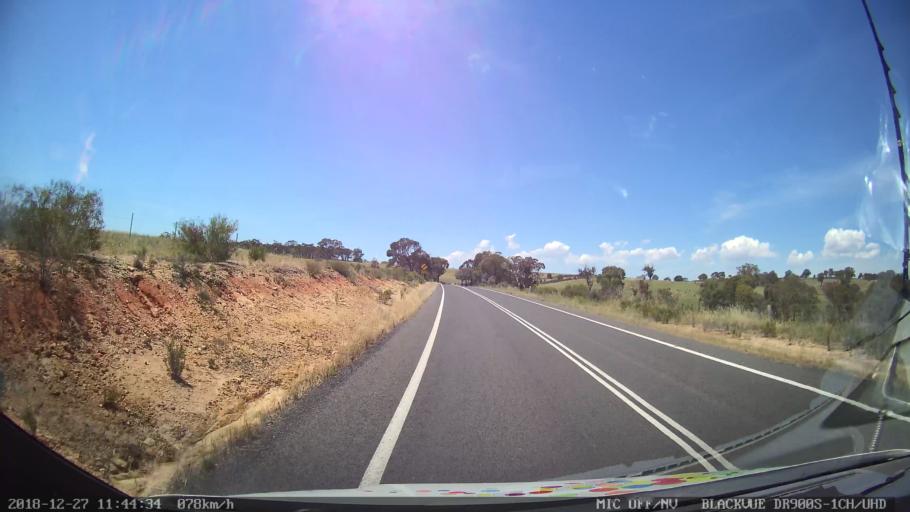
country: AU
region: New South Wales
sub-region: Bathurst Regional
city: Perthville
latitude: -33.5737
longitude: 149.4754
